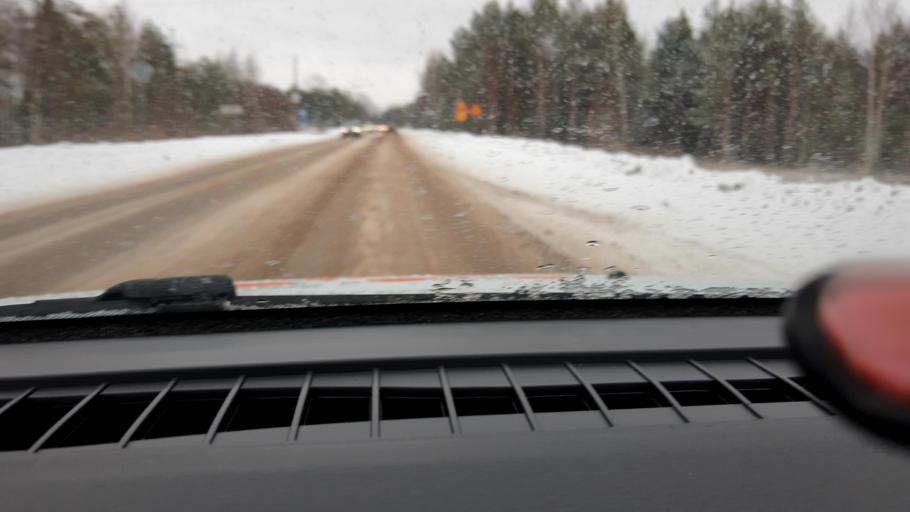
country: RU
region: Nizjnij Novgorod
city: Bor
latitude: 56.3257
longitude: 44.1371
